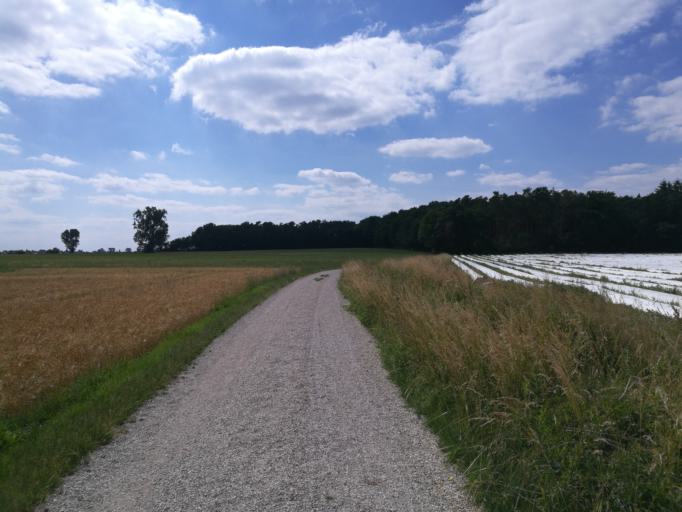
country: DE
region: Bavaria
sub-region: Regierungsbezirk Mittelfranken
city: Seukendorf
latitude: 49.4934
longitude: 10.9016
